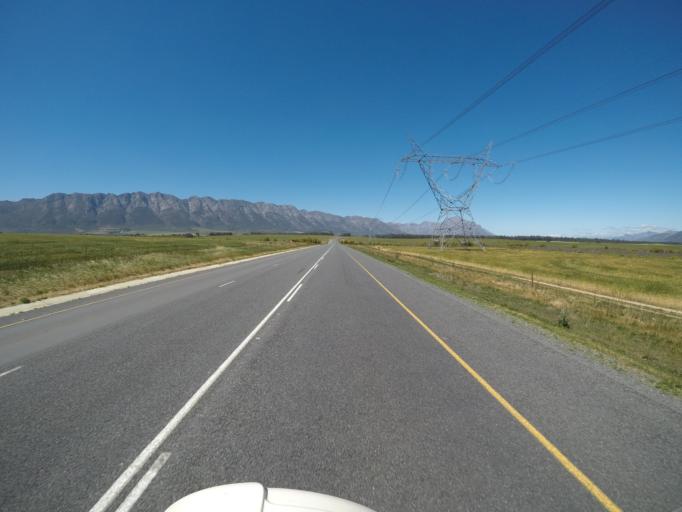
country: ZA
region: Western Cape
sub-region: Cape Winelands District Municipality
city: Ceres
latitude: -33.3226
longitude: 19.1441
